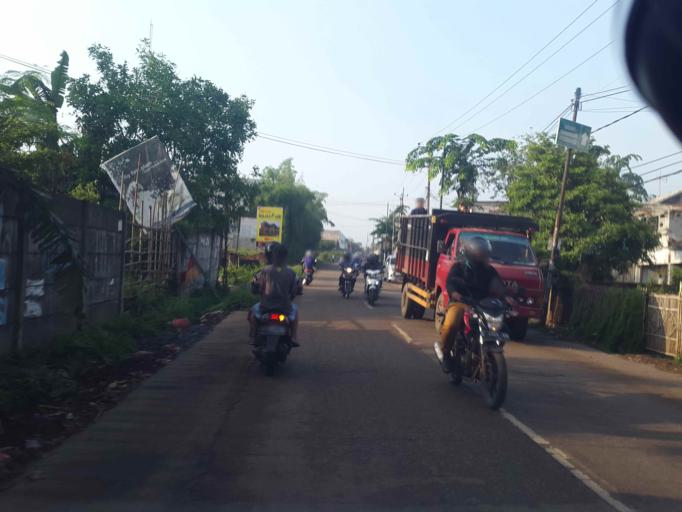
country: ID
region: West Java
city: Cikarang
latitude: -6.3165
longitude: 107.0614
